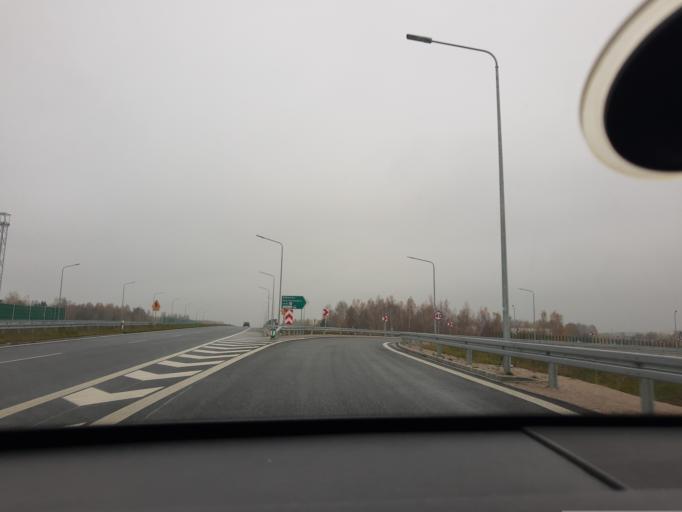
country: PL
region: Lodz Voivodeship
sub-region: Powiat pabianicki
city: Konstantynow Lodzki
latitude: 51.7300
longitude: 19.3559
